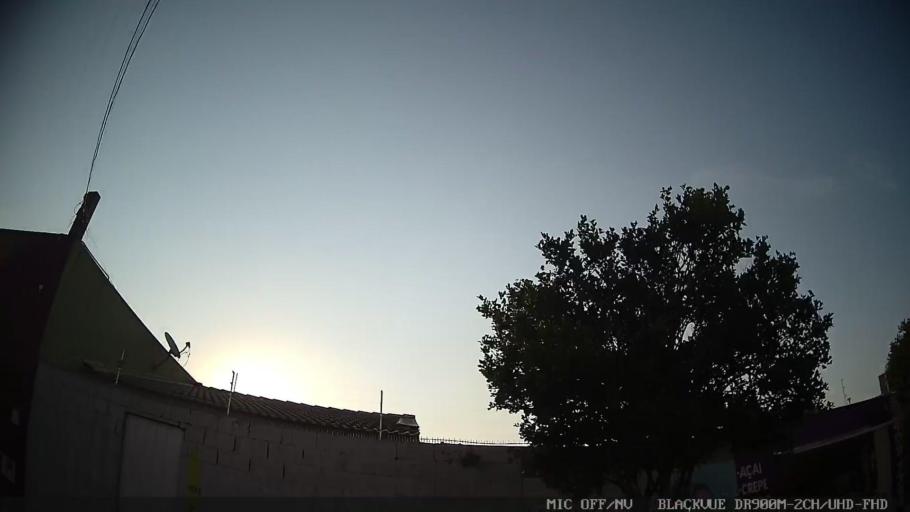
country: BR
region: Sao Paulo
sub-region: Itatiba
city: Itatiba
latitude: -23.0046
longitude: -46.8195
